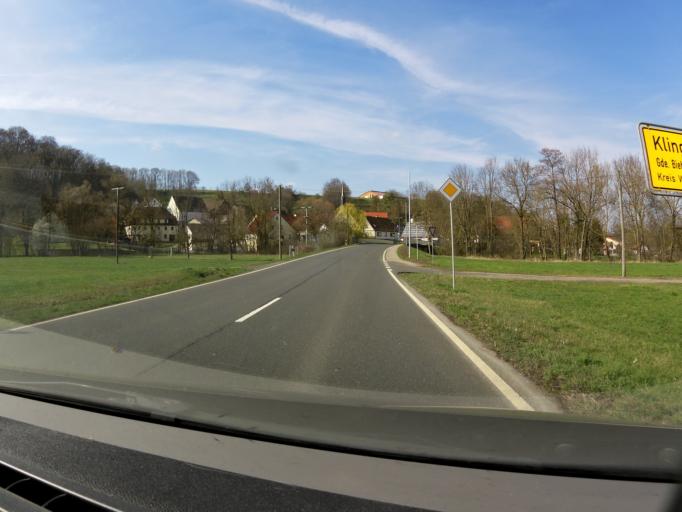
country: DE
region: Baden-Wuerttemberg
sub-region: Regierungsbezirk Stuttgart
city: Creglingen
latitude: 49.4905
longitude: 10.0179
